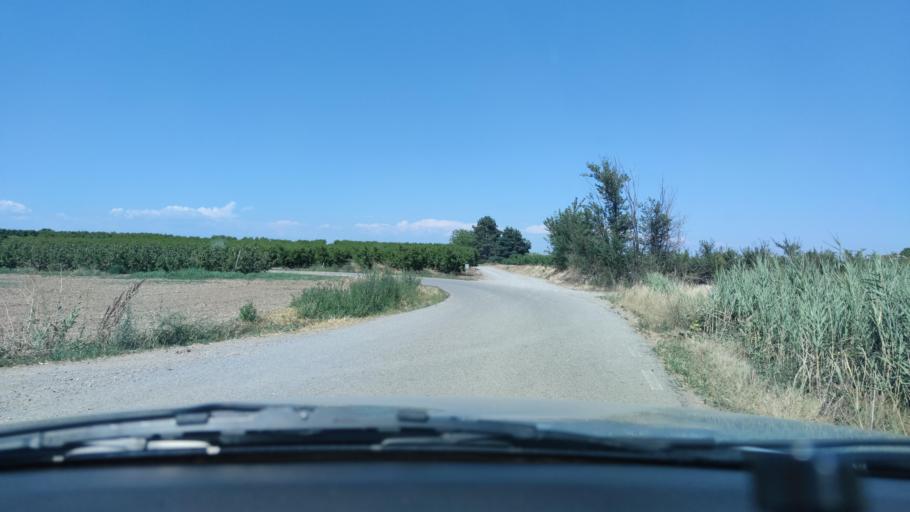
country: ES
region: Catalonia
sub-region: Provincia de Lleida
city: Torrefarrera
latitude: 41.6797
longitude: 0.6165
